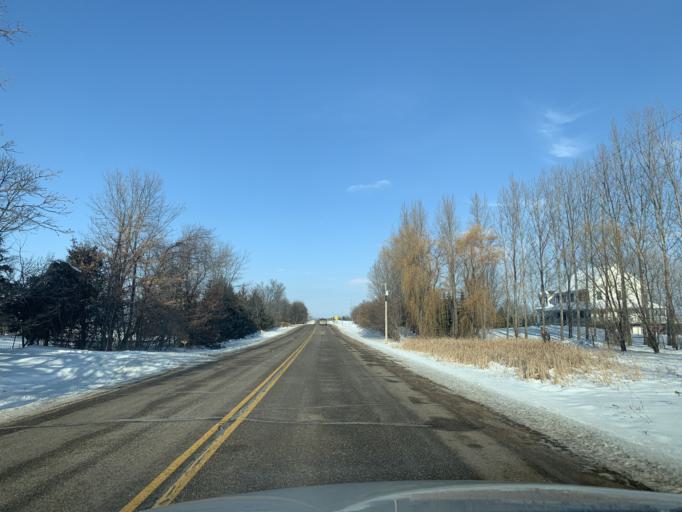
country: US
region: Minnesota
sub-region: Wright County
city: Buffalo
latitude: 45.1985
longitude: -93.8271
